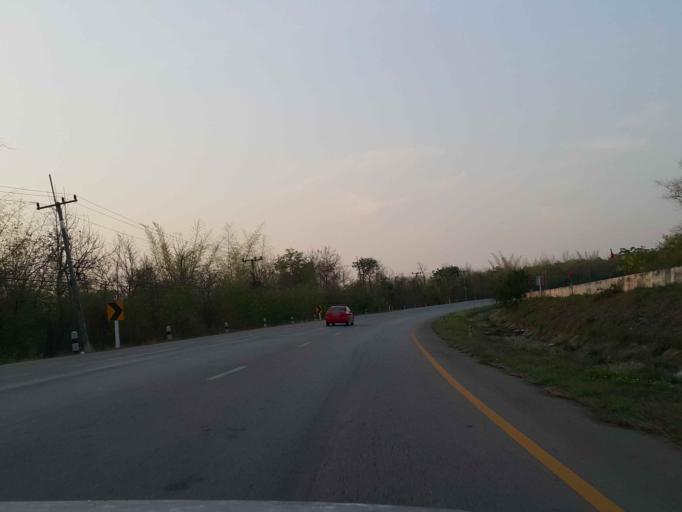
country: TH
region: Lampang
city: Sop Prap
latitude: 17.9676
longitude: 99.3525
